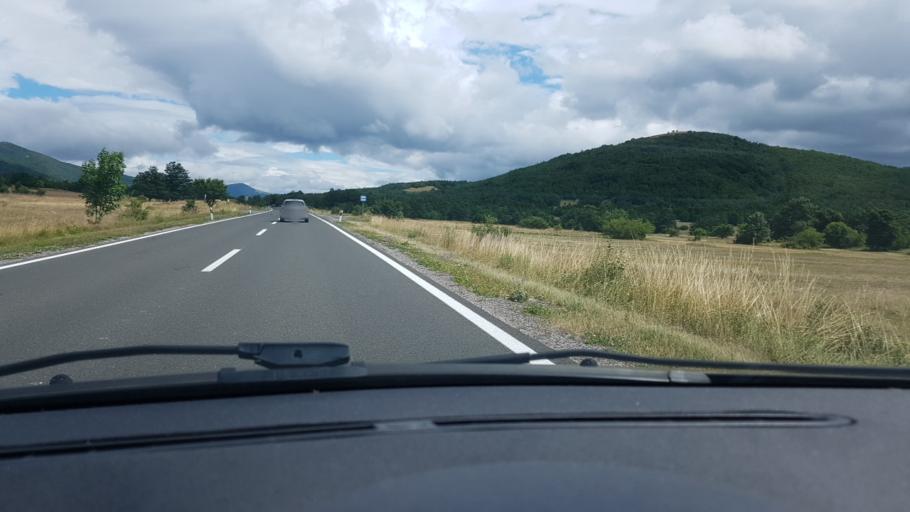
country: HR
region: Zadarska
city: Gracac
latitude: 44.4620
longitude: 15.8077
